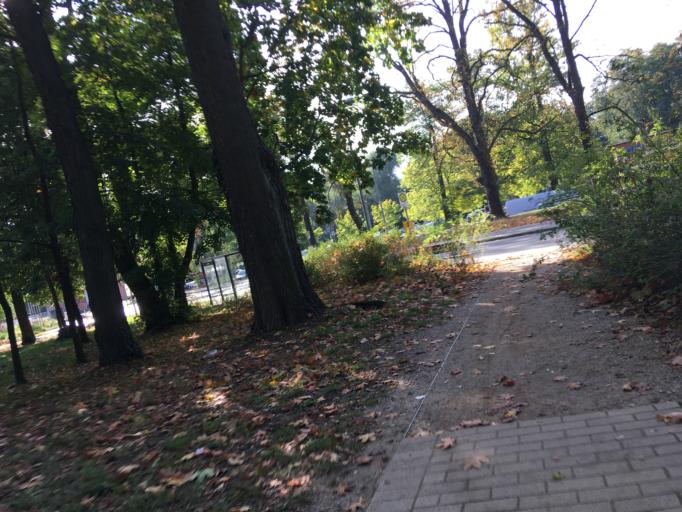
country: DE
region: Brandenburg
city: Hoppegarten
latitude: 52.5160
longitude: 13.6713
